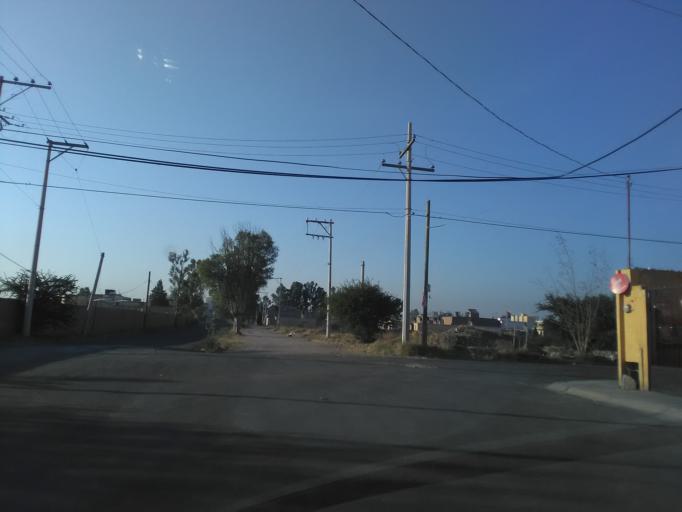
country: MX
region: Durango
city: Victoria de Durango
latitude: 24.0589
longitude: -104.6189
